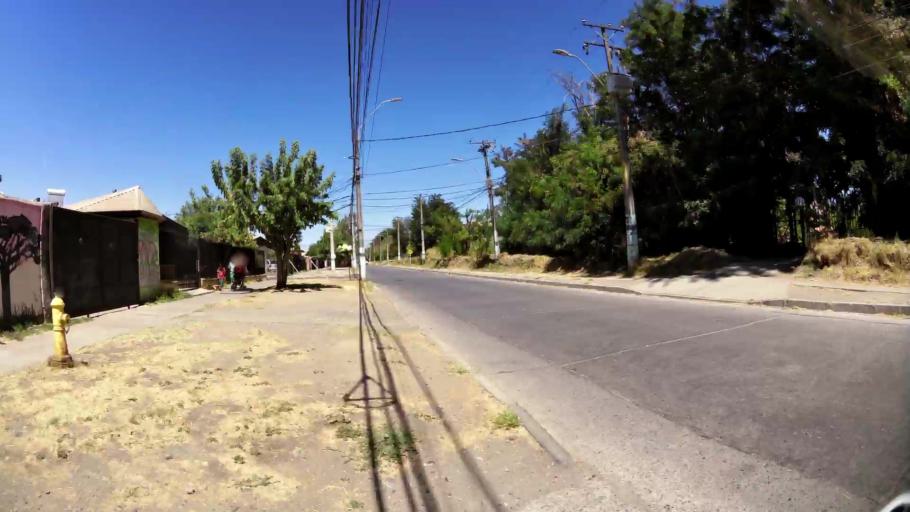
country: CL
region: O'Higgins
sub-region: Provincia de Cachapoal
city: Rancagua
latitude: -34.1560
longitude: -70.7513
